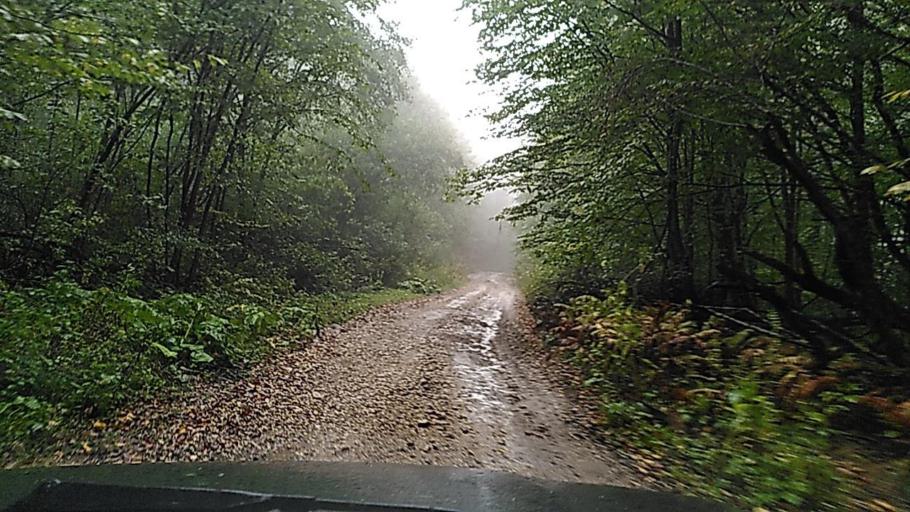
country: RU
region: Kabardino-Balkariya
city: Belaya Rechka
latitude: 43.3770
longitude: 43.4323
